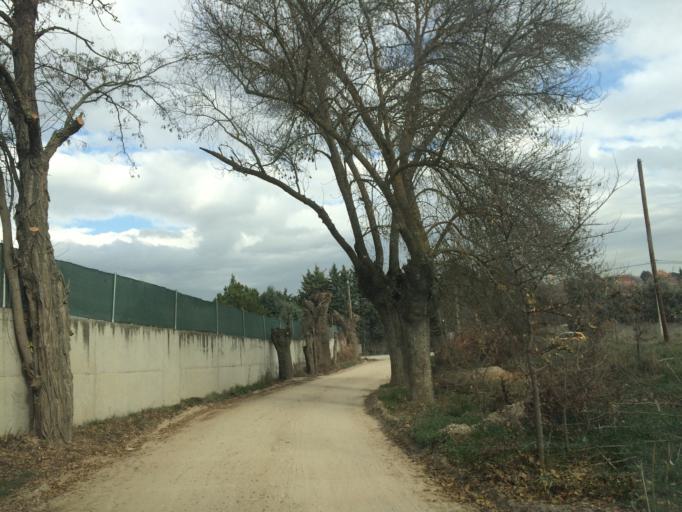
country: ES
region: Madrid
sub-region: Provincia de Madrid
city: Arroyomolinos
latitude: 40.3111
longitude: -3.9477
